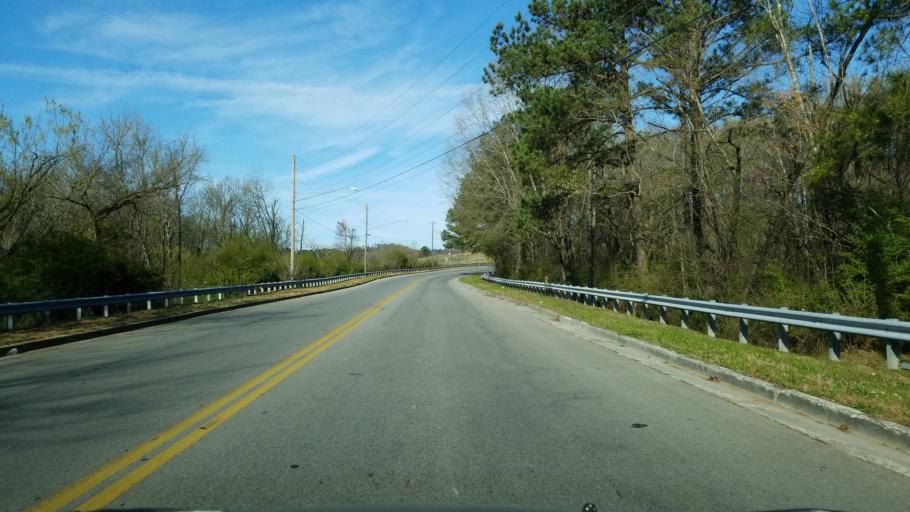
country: US
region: Tennessee
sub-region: Hamilton County
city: East Chattanooga
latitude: 35.0507
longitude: -85.2102
